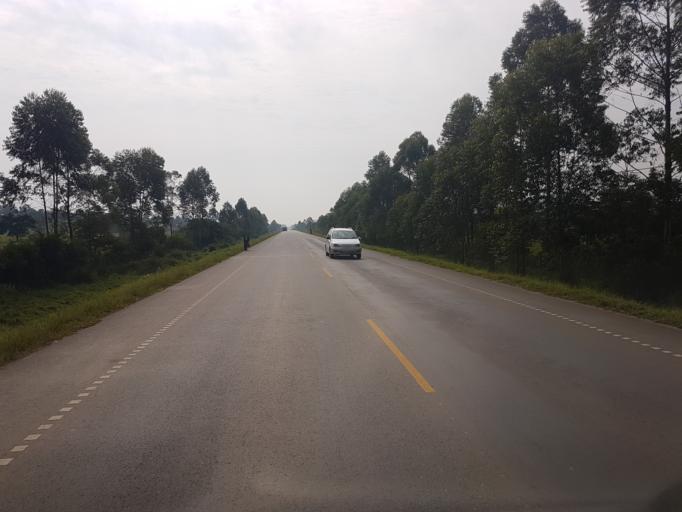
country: UG
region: Western Region
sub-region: Sheema District
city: Kibingo
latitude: -0.6471
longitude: 30.4905
